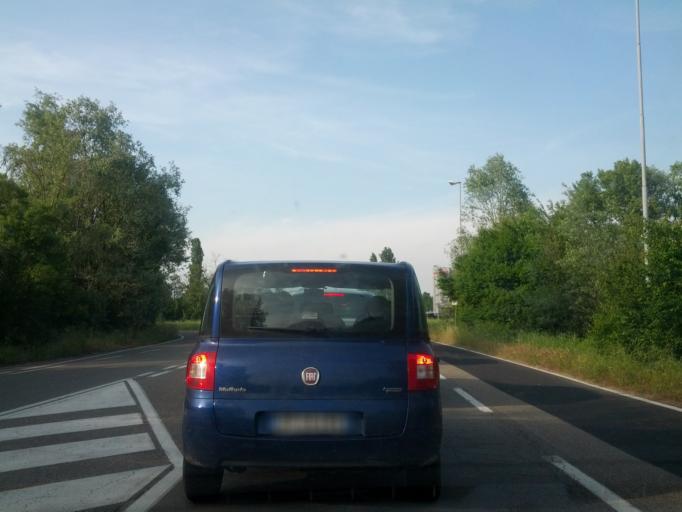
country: IT
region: Emilia-Romagna
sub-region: Provincia di Reggio Emilia
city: Bagnolo in Piano
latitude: 44.7667
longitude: 10.6643
